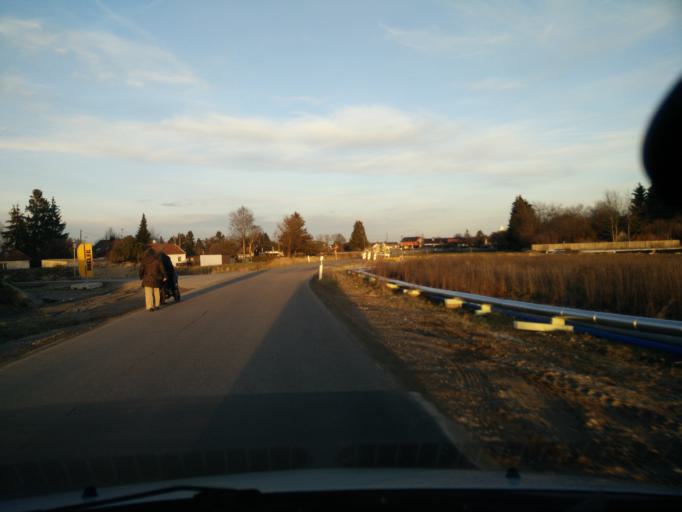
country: DE
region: Bavaria
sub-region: Upper Bavaria
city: Germering
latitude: 48.1550
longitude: 11.4065
